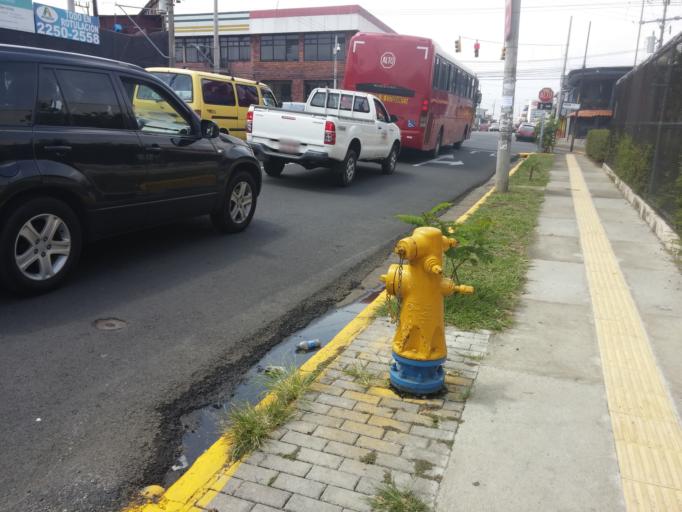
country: CR
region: Heredia
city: Heredia
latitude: 9.9988
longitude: -84.1236
